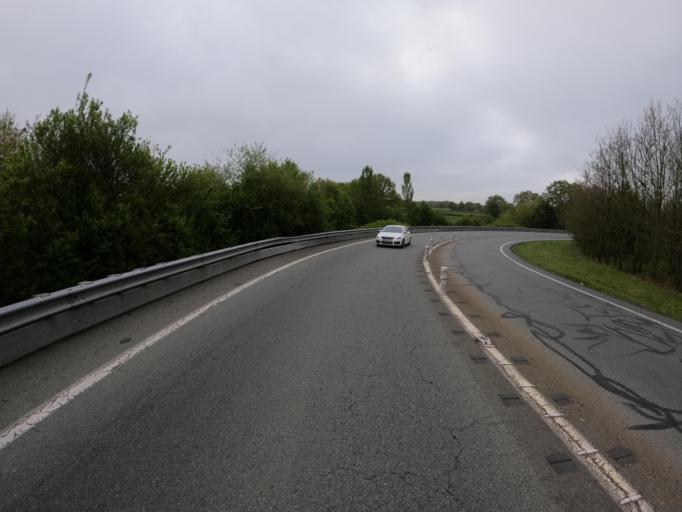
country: FR
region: Pays de la Loire
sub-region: Departement de Maine-et-Loire
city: Nuaille
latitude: 47.0863
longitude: -0.8230
